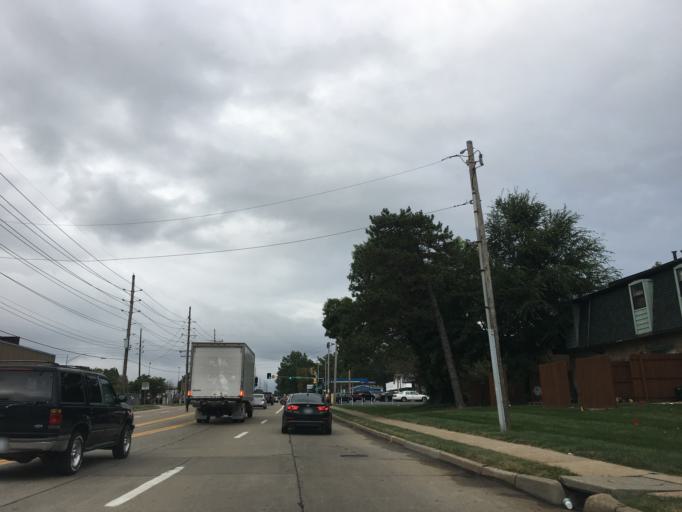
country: US
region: Missouri
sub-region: Saint Louis County
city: Berkeley
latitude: 38.7614
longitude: -90.3371
